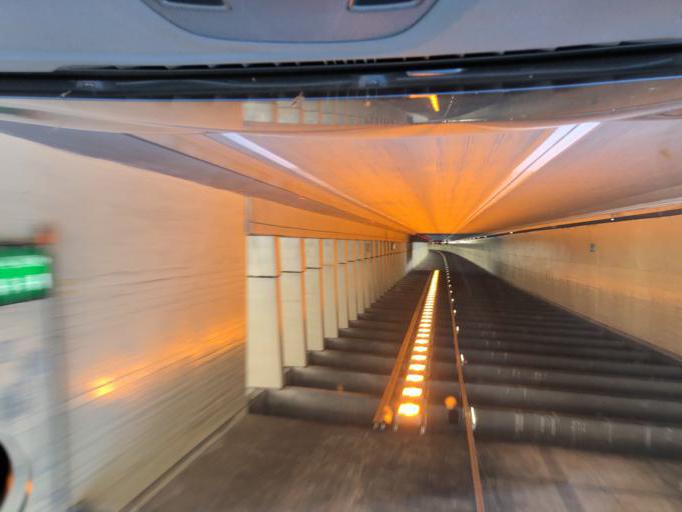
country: AT
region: Tyrol
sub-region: Politischer Bezirk Landeck
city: Sankt Anton am Arlberg
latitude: 47.1413
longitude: 10.3130
